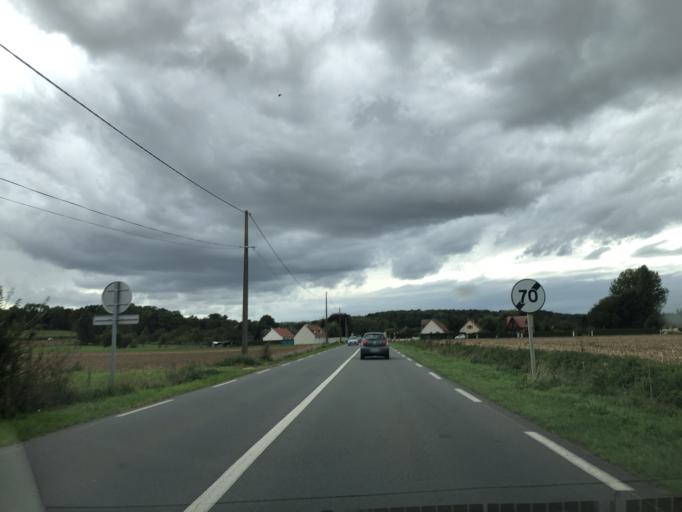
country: FR
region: Picardie
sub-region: Departement de la Somme
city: Abbeville
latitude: 50.1090
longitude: 1.7793
